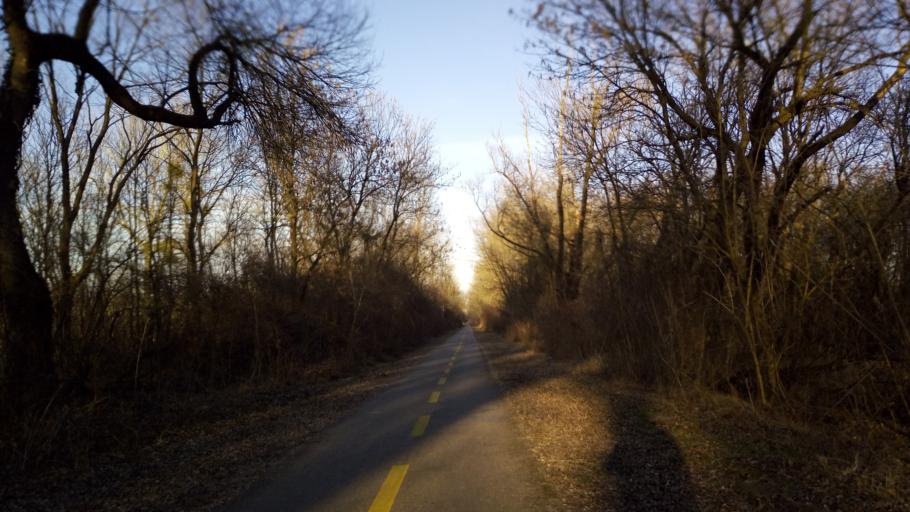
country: HU
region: Baranya
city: Pellerd
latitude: 46.0409
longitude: 18.1789
